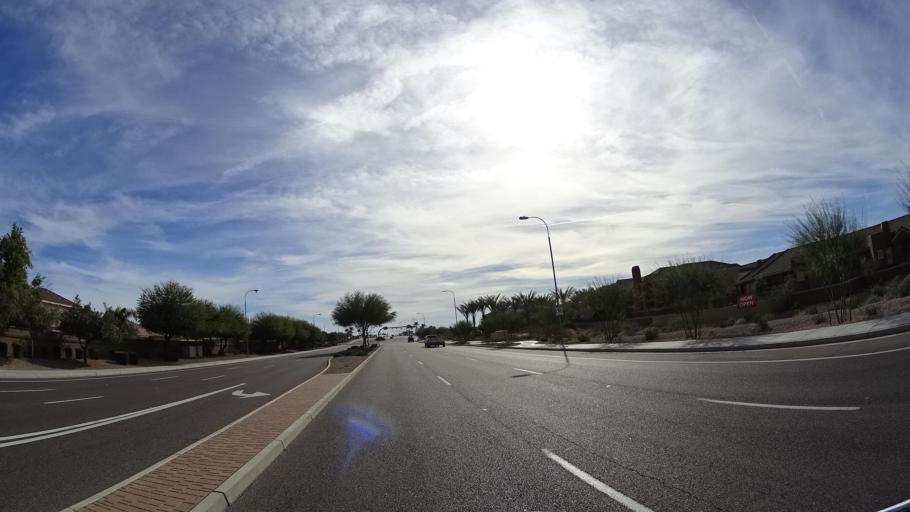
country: US
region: Arizona
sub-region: Maricopa County
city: Chandler
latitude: 33.2865
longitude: -111.8070
